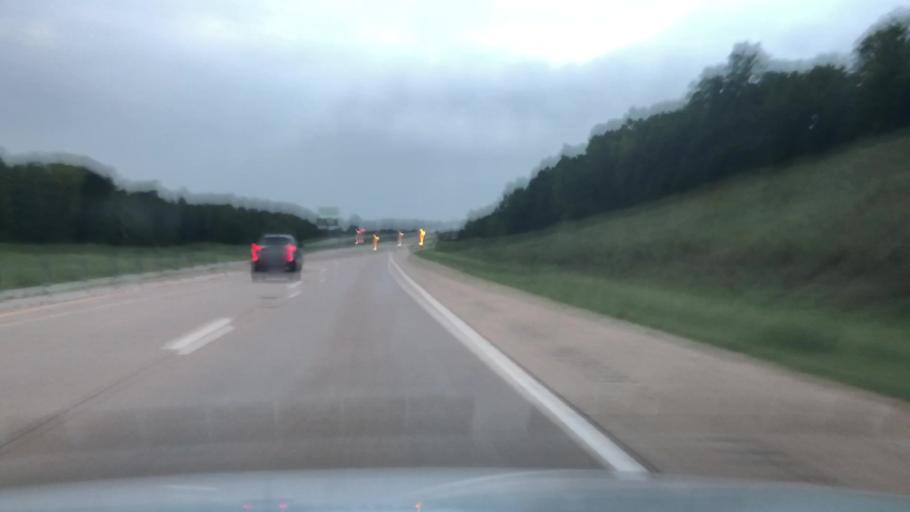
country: US
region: Oklahoma
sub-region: Osage County
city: Skiatook
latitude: 36.5265
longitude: -95.9270
